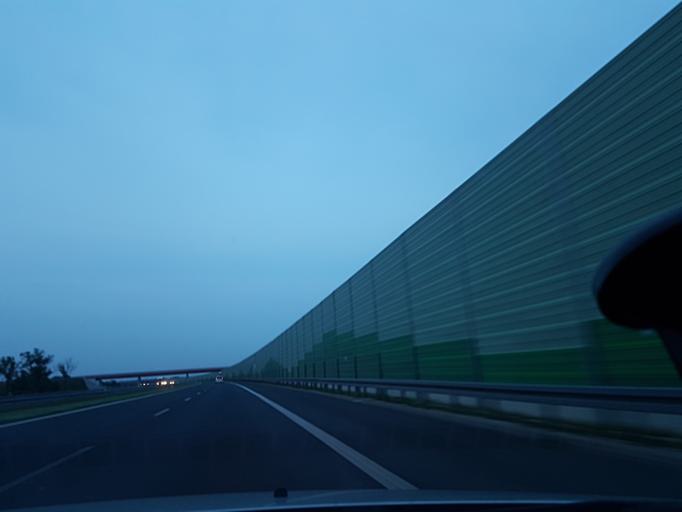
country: PL
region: Lodz Voivodeship
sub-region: Powiat kutnowski
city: Krzyzanow
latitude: 52.1507
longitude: 19.4814
